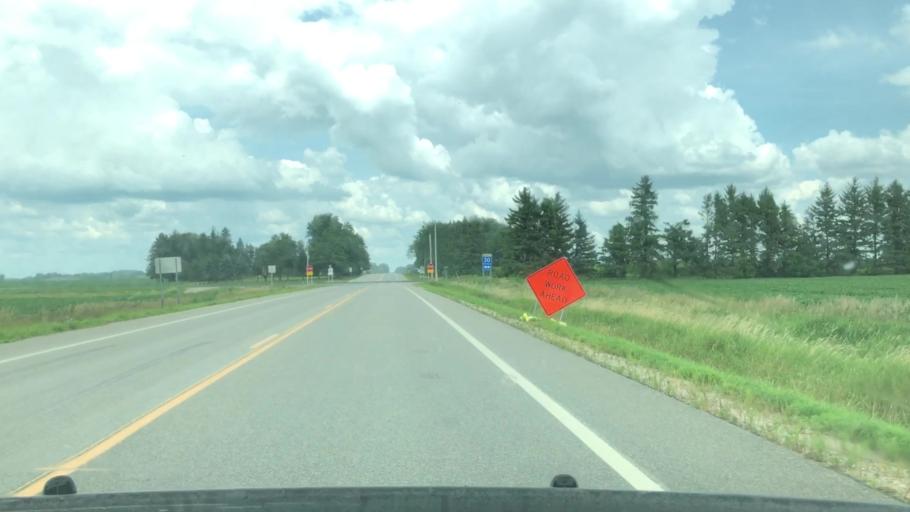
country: US
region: Minnesota
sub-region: Olmsted County
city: Stewartville
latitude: 43.8906
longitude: -92.5285
